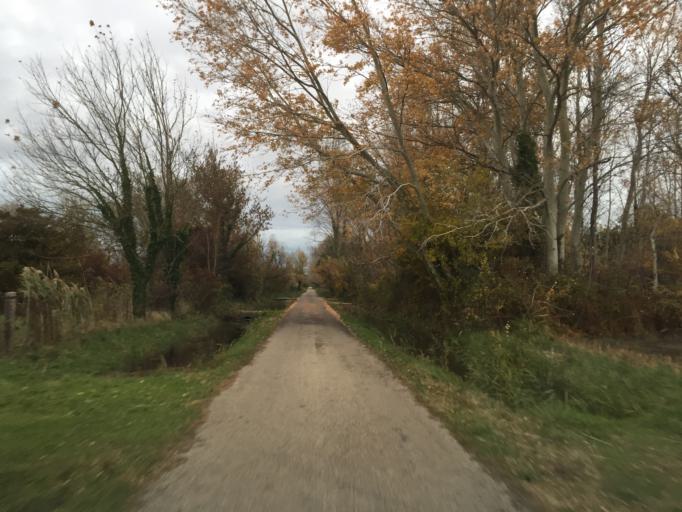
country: FR
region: Provence-Alpes-Cote d'Azur
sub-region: Departement du Vaucluse
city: Courthezon
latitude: 44.0878
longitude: 4.8648
